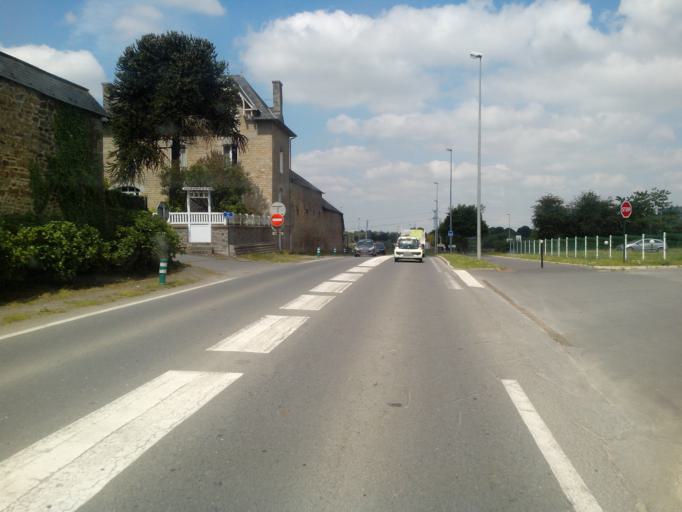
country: FR
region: Brittany
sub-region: Departement d'Ille-et-Vilaine
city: Lecousse
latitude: 48.3624
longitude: -1.2261
